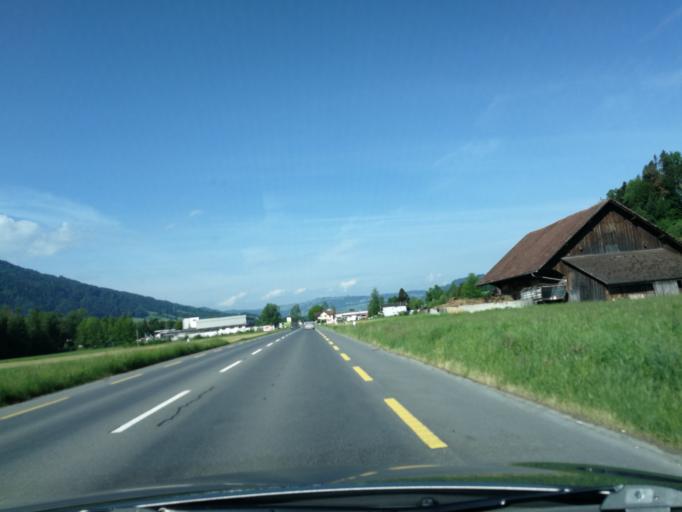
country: CH
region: Lucerne
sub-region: Lucerne-Stadt District
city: Littau
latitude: 47.0507
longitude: 8.2421
